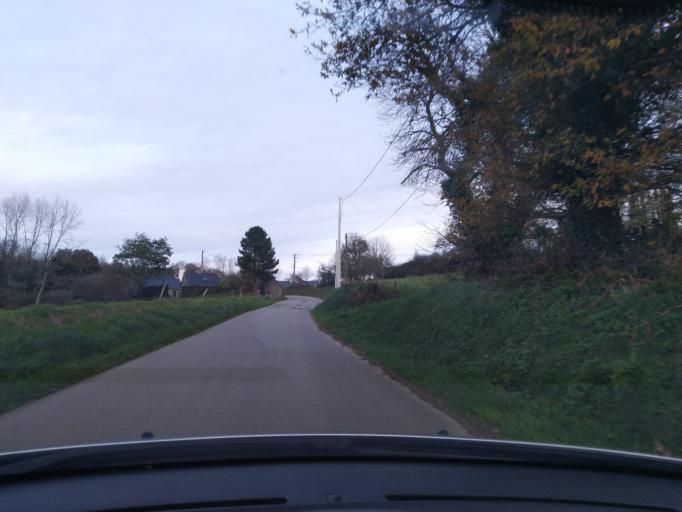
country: FR
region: Brittany
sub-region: Departement du Finistere
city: Guerlesquin
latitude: 48.5619
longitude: -3.6165
